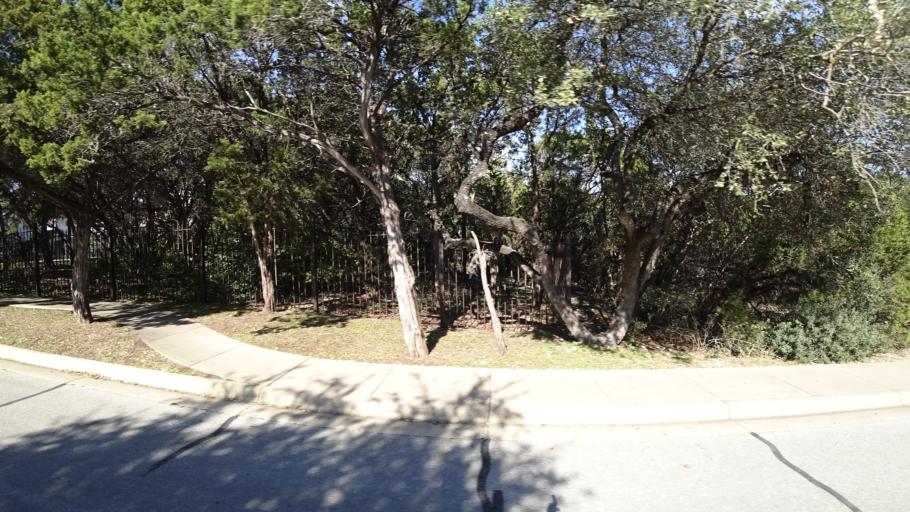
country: US
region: Texas
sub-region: Williamson County
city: Jollyville
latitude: 30.3770
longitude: -97.7701
